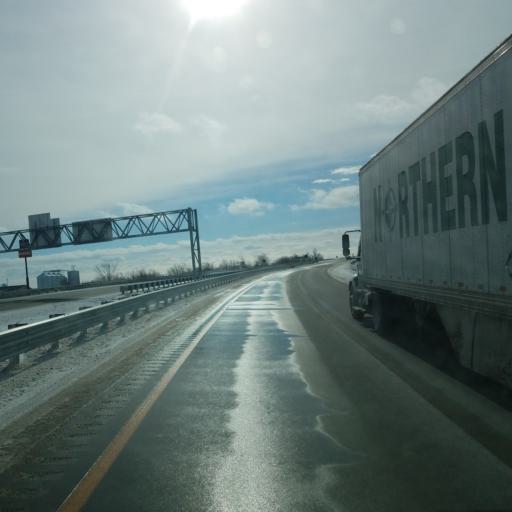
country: US
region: Michigan
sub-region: Gratiot County
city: Ithaca
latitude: 43.2929
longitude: -84.5826
